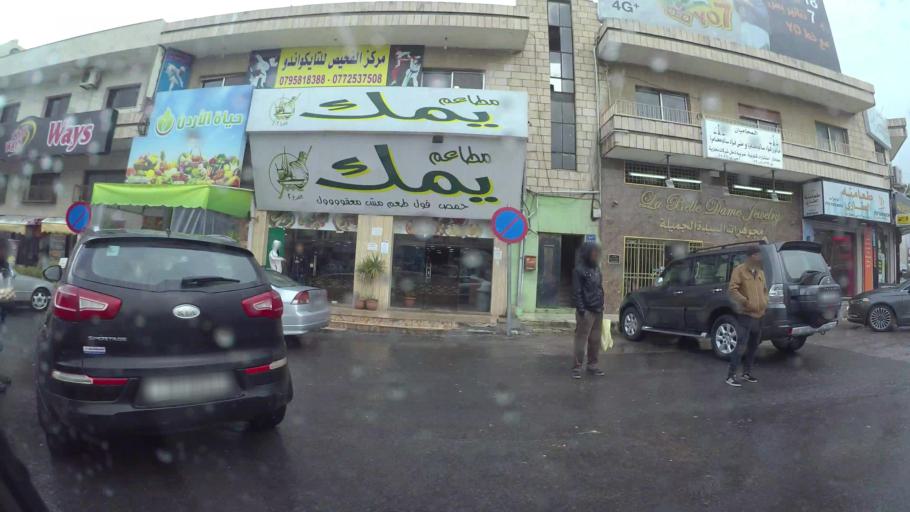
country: JO
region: Amman
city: Wadi as Sir
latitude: 32.0041
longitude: 35.7847
